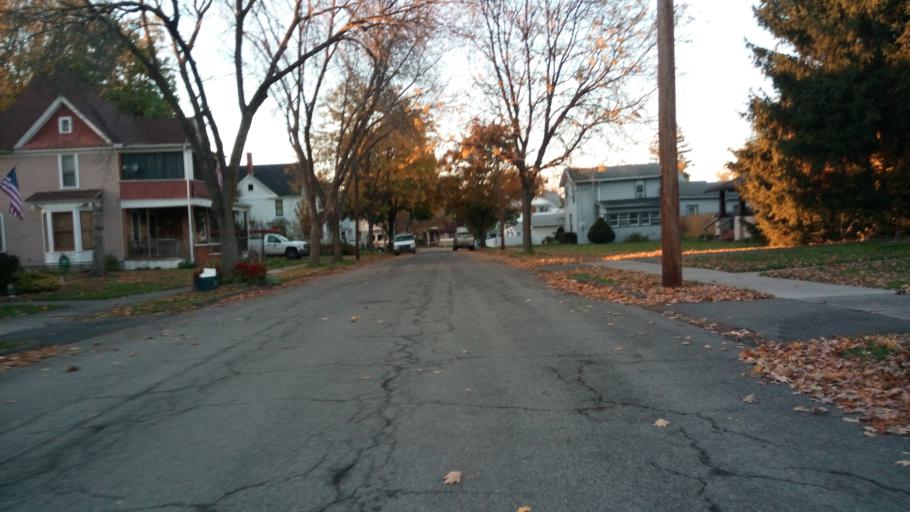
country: US
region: New York
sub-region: Chemung County
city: Elmira
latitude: 42.0772
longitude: -76.8082
